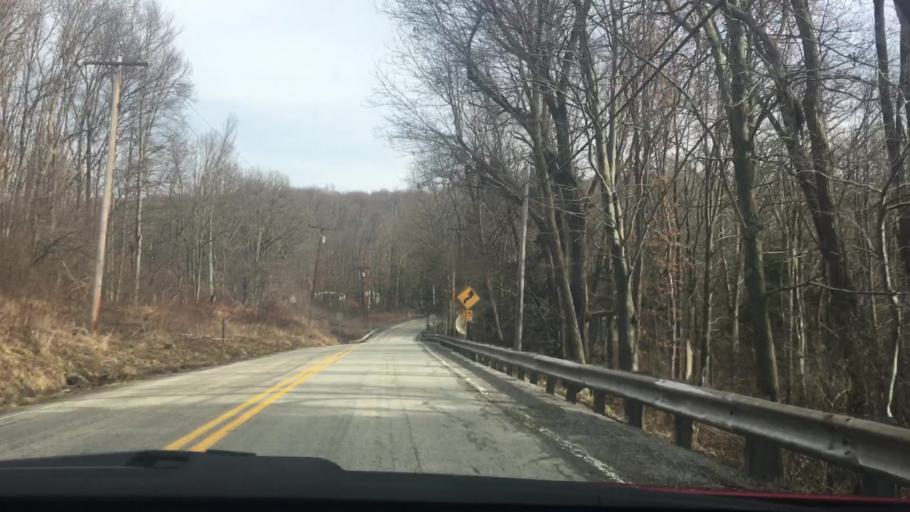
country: US
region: Pennsylvania
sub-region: Fayette County
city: Hopwood
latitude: 39.8227
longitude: -79.5464
